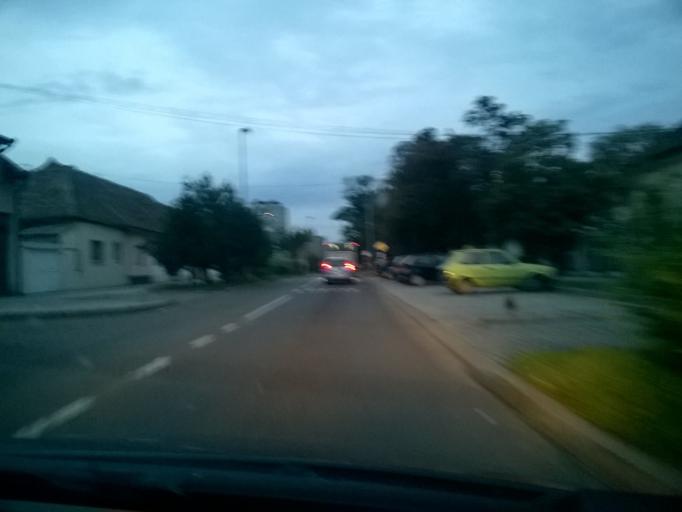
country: RS
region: Autonomna Pokrajina Vojvodina
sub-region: Juznobanatski Okrug
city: Pancevo
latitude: 44.8619
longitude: 20.6477
